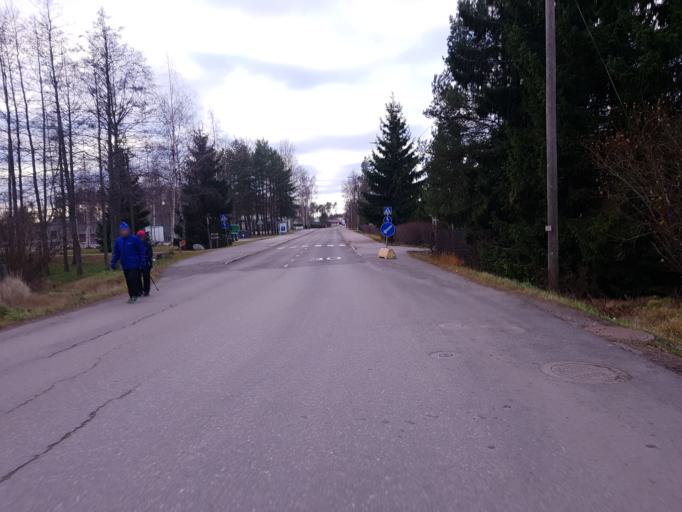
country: FI
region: Uusimaa
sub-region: Helsinki
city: Helsinki
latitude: 60.2801
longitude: 24.9206
